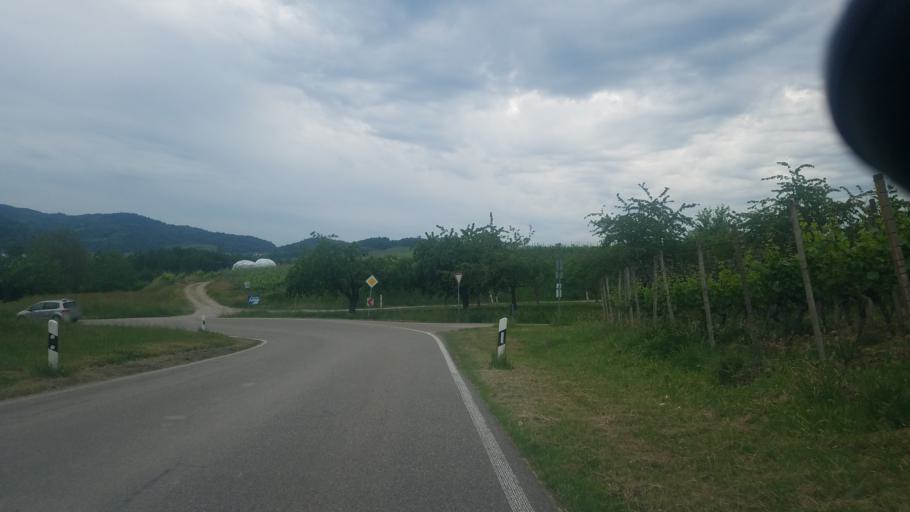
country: DE
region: Baden-Wuerttemberg
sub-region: Freiburg Region
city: Kappelrodeck
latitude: 48.6037
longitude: 8.1076
